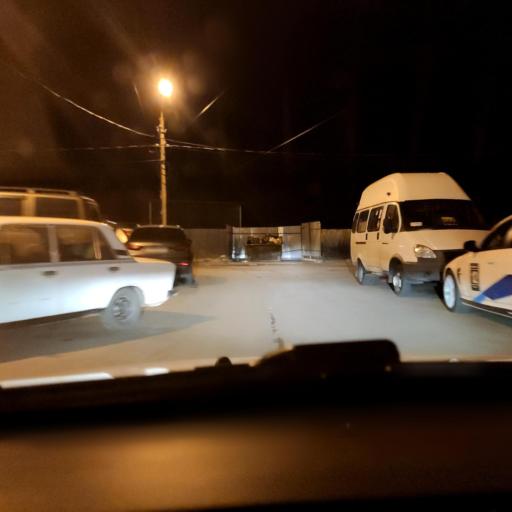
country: RU
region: Voronezj
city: Podgornoye
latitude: 51.7257
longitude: 39.1909
